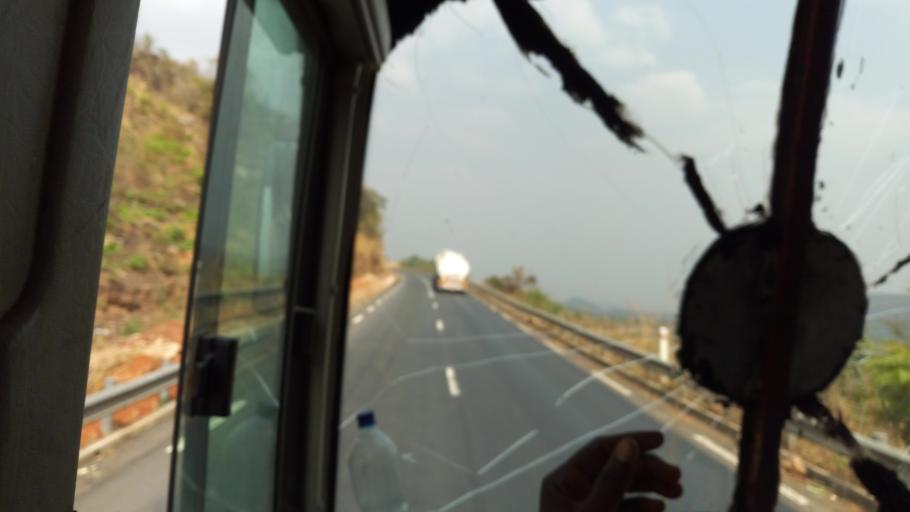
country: TG
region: Kara
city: Bafilo
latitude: 9.2521
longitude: 1.2185
